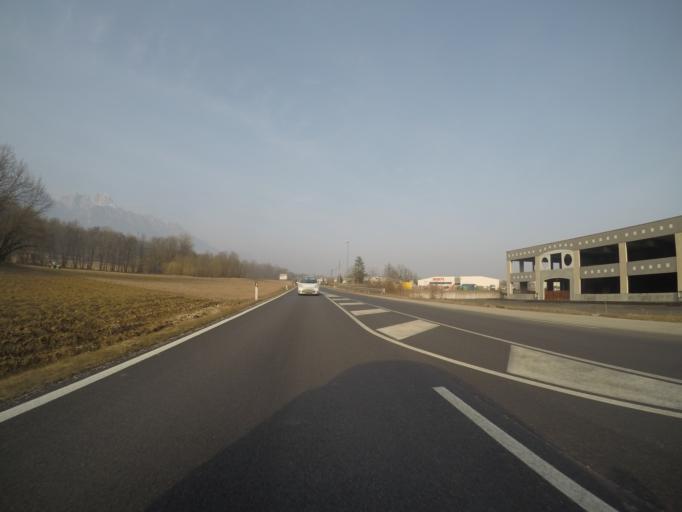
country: IT
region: Veneto
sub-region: Provincia di Belluno
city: Lentiai
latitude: 46.0694
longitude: 12.0159
